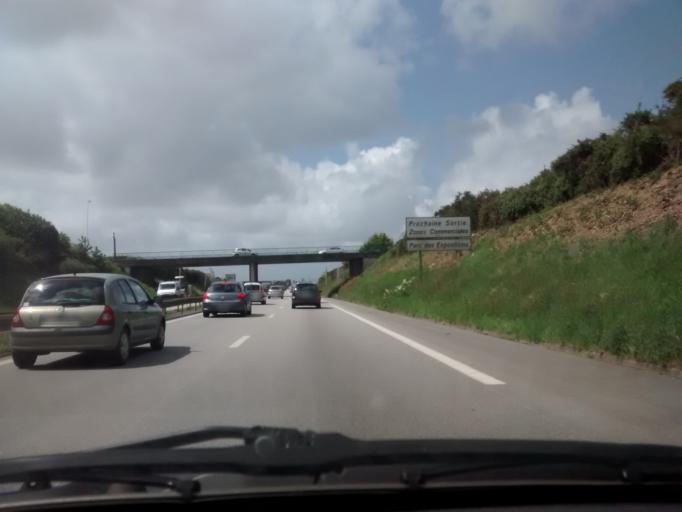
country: FR
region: Brittany
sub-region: Departement du Morbihan
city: Vannes
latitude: 47.6664
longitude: -2.7819
